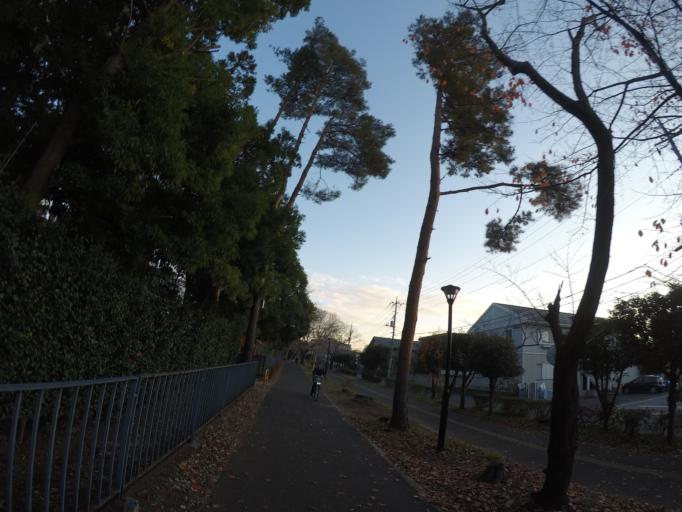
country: JP
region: Ibaraki
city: Naka
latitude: 36.0656
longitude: 140.1239
